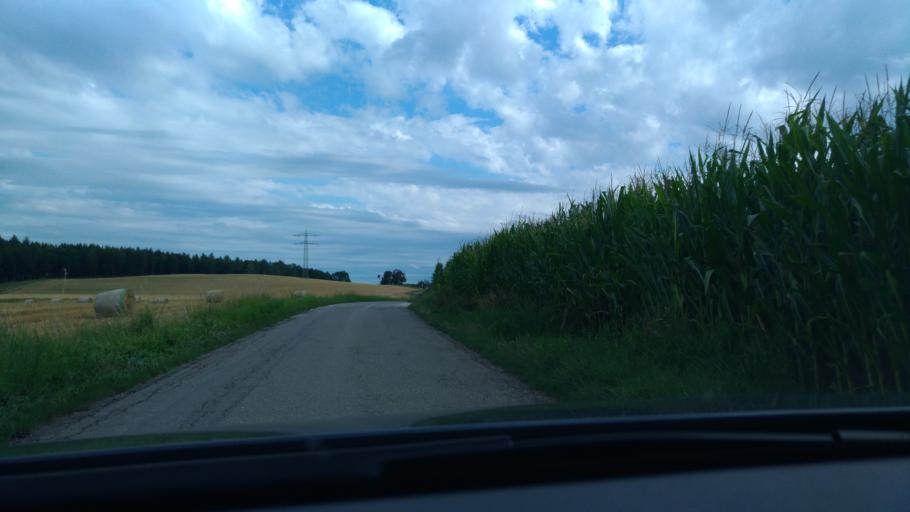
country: DE
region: Baden-Wuerttemberg
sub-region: Tuebingen Region
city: Sipplingen
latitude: 47.8019
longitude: 9.1222
